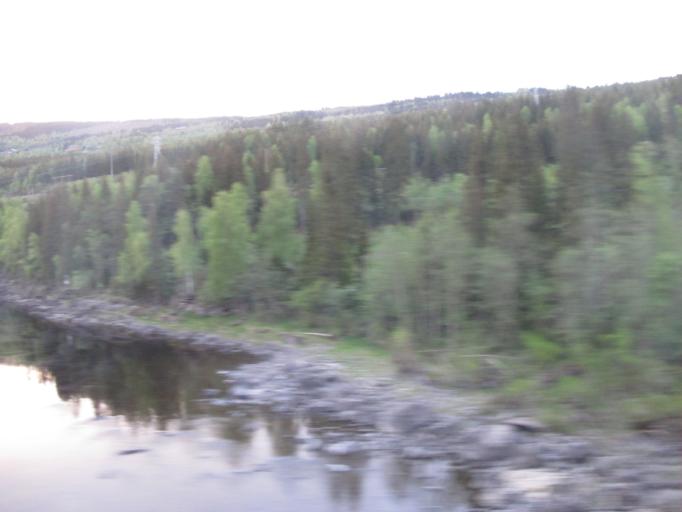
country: NO
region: Oppland
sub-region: Lillehammer
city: Lillehammer
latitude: 61.2138
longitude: 10.4377
